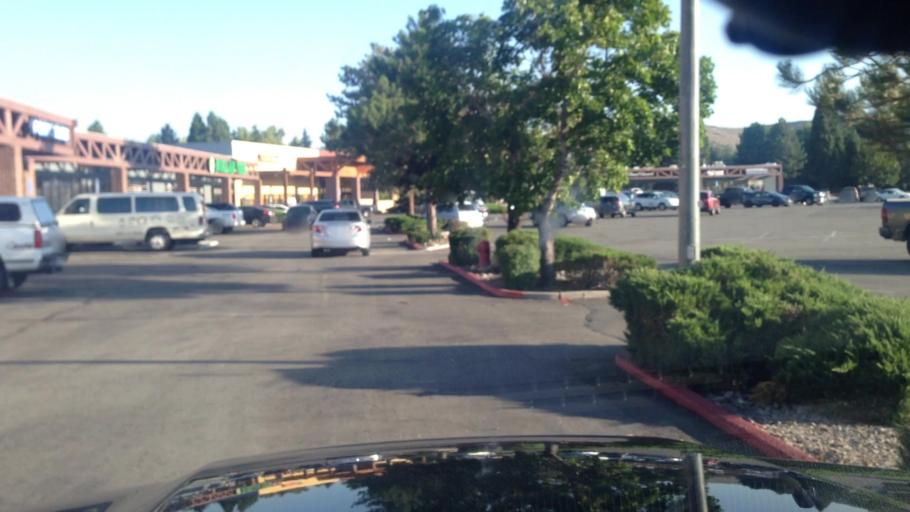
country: US
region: Nevada
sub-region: Washoe County
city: Sparks
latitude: 39.4852
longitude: -119.7467
